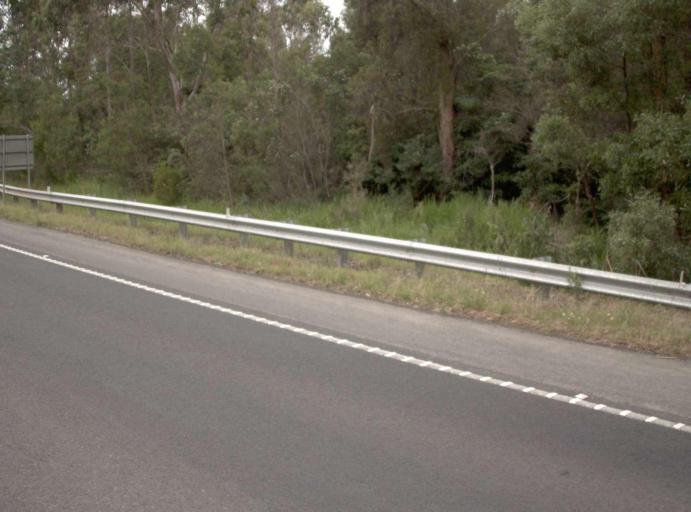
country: AU
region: Victoria
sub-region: Bass Coast
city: North Wonthaggi
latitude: -38.5490
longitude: 145.9508
